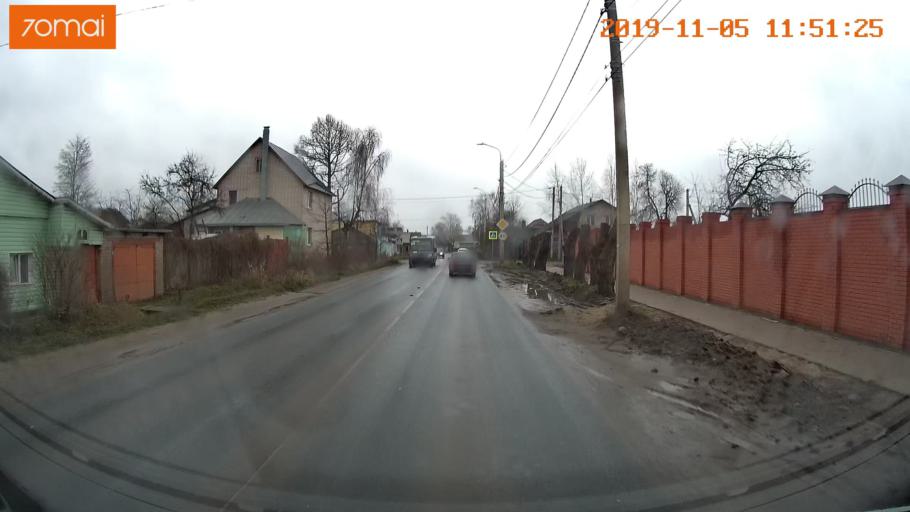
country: RU
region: Ivanovo
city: Bogorodskoye
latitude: 57.0058
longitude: 41.0271
